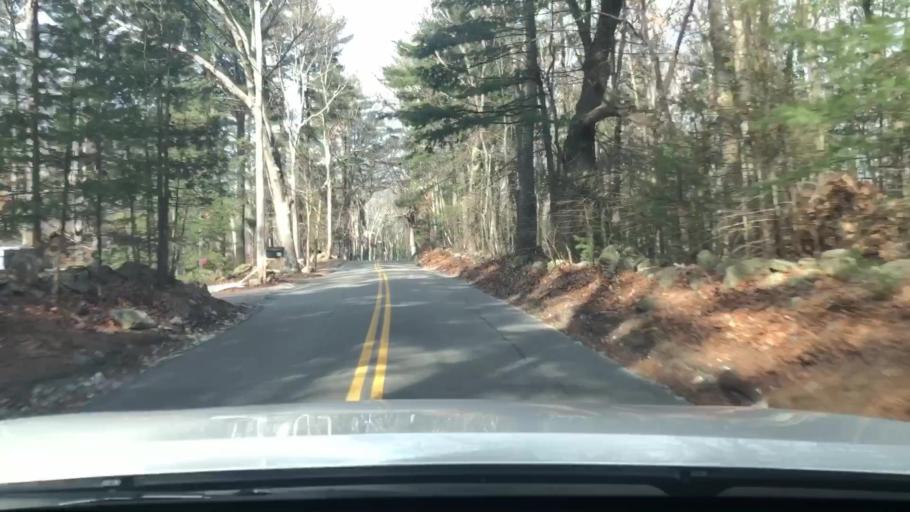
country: US
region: Massachusetts
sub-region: Norfolk County
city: Bellingham
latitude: 42.1075
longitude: -71.4962
